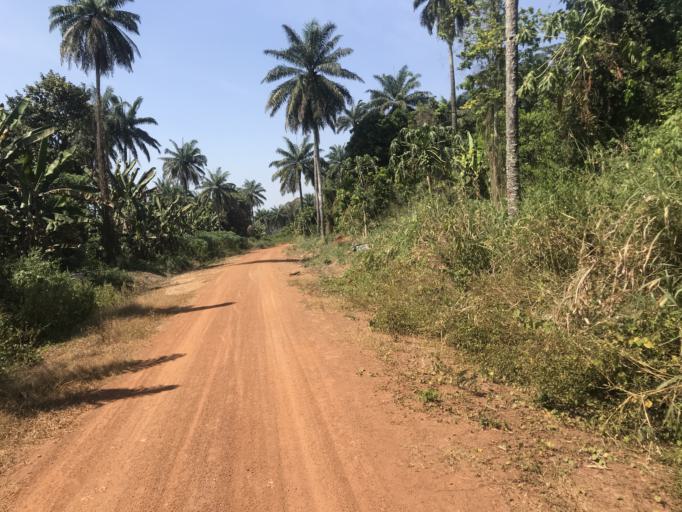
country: NG
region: Osun
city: Ikirun
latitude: 7.9329
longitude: 4.6247
